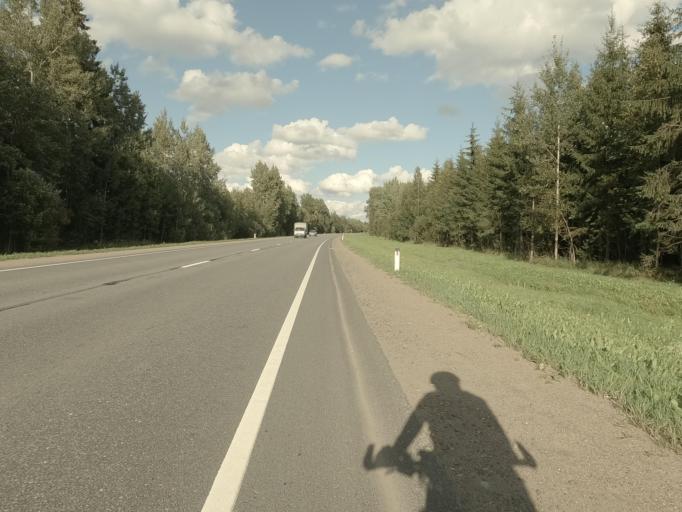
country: RU
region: Leningrad
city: Nikol'skoye
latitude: 59.6672
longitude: 30.8869
